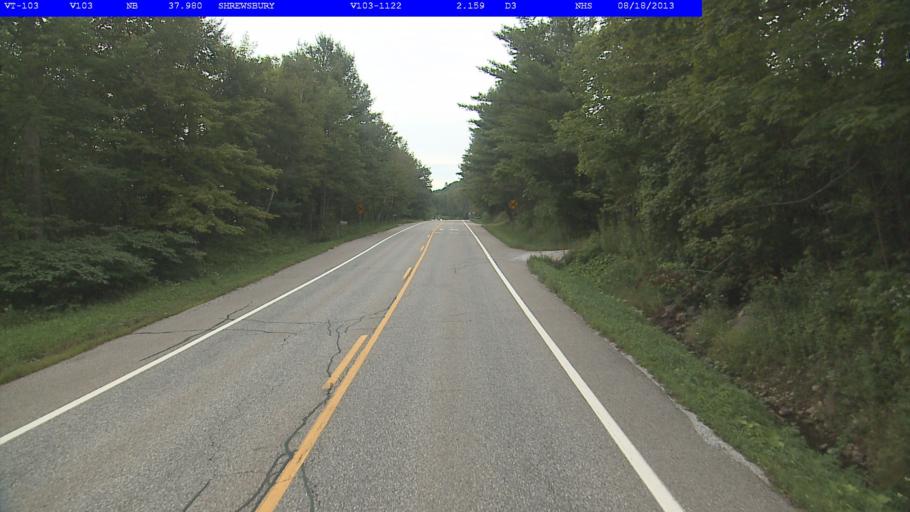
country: US
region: Vermont
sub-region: Rutland County
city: Rutland
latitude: 43.5038
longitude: -72.9012
